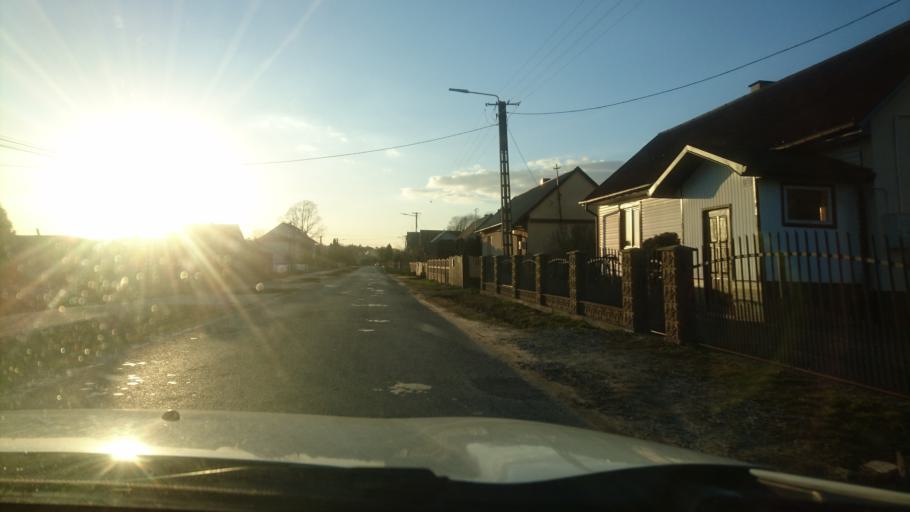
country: PL
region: Swietokrzyskie
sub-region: Powiat kielecki
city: Morawica
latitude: 50.7433
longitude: 20.6864
